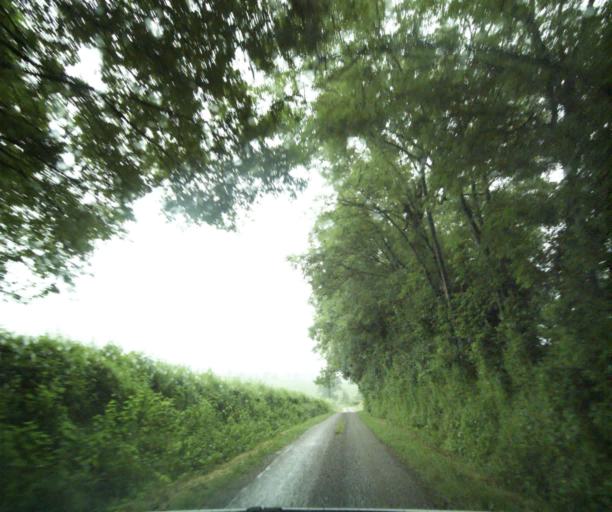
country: FR
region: Bourgogne
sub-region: Departement de Saone-et-Loire
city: Charolles
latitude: 46.4146
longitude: 4.2165
